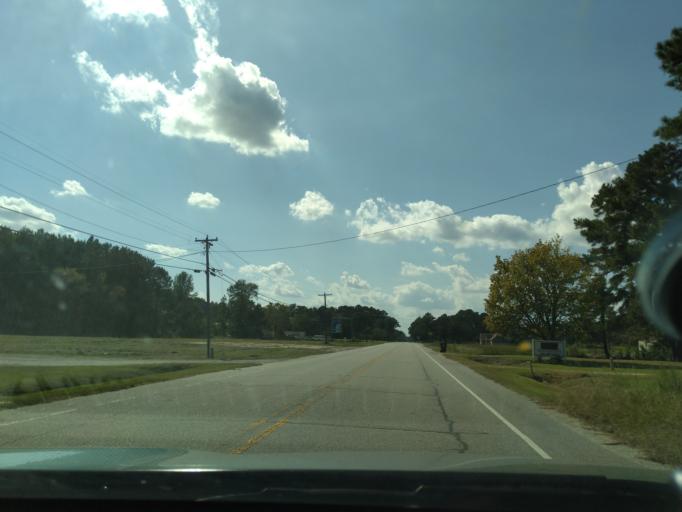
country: US
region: North Carolina
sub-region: Martin County
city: Robersonville
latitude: 35.8272
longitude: -77.2425
